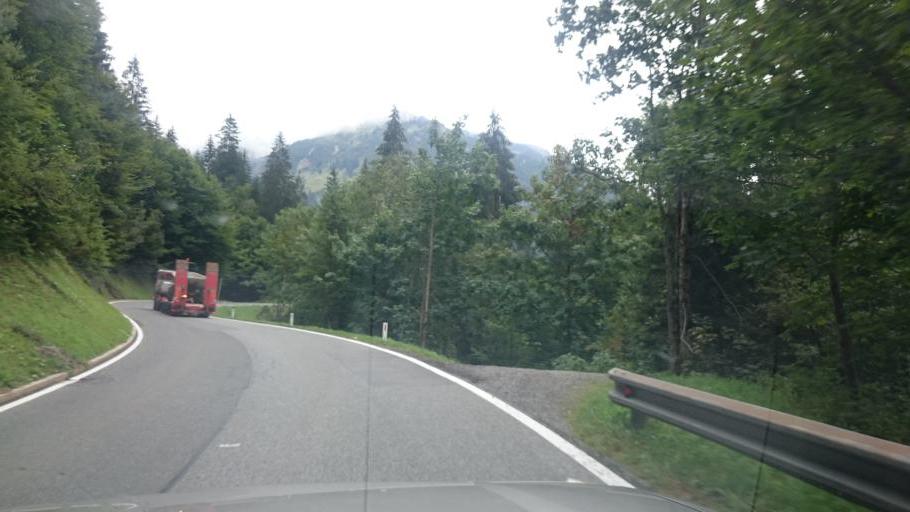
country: AT
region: Vorarlberg
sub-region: Politischer Bezirk Bregenz
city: Schoppernau
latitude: 47.2863
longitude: 10.0473
